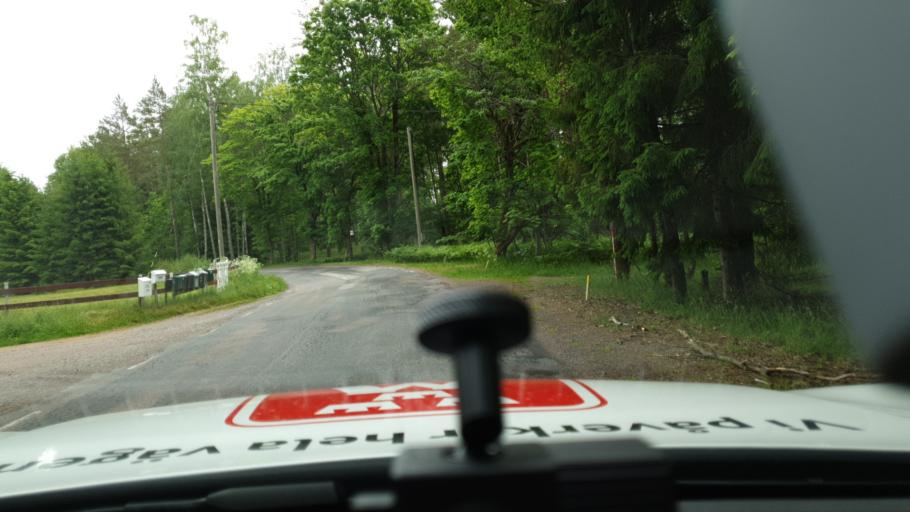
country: SE
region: Vaestra Goetaland
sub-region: Karlsborgs Kommun
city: Molltorp
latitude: 58.4182
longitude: 14.3405
